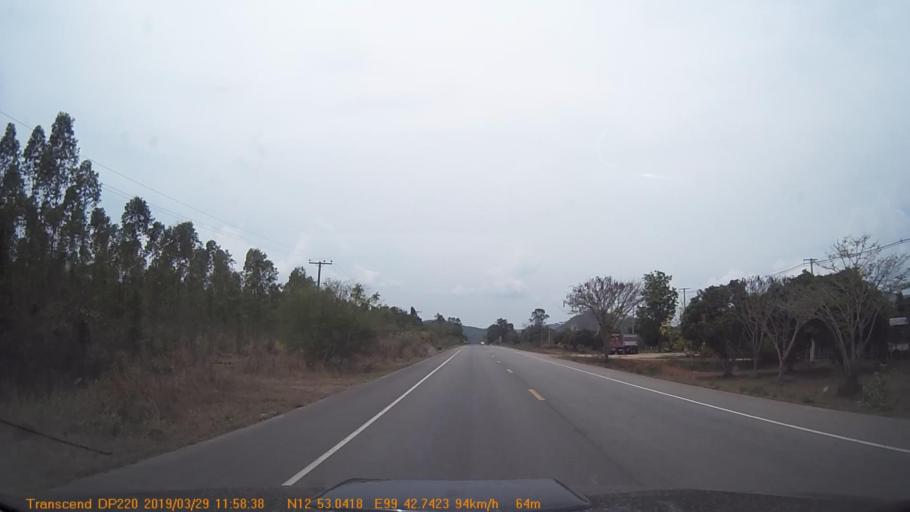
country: TH
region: Phetchaburi
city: Kaeng Krachan
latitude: 12.8836
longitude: 99.7121
